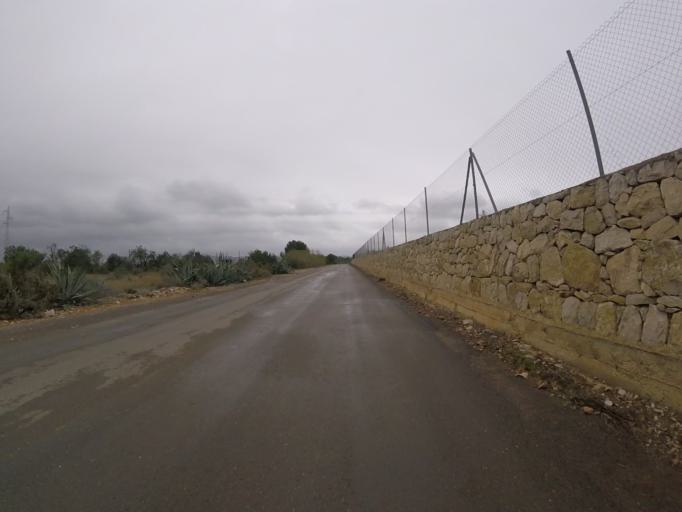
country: ES
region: Valencia
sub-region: Provincia de Castello
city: Alcoceber
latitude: 40.2394
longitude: 0.2496
